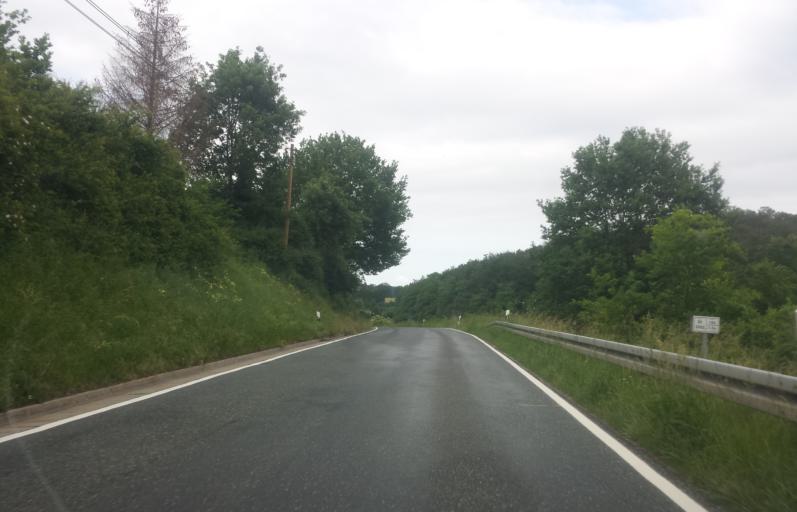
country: DE
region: Bavaria
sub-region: Upper Franconia
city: Schlusselfeld
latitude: 49.7645
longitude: 10.6277
